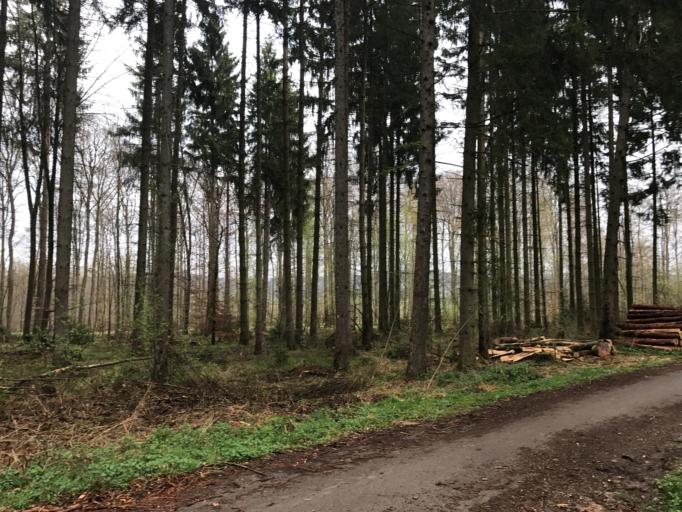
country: DE
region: Baden-Wuerttemberg
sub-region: Regierungsbezirk Stuttgart
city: Hochdorf
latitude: 48.6868
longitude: 9.4487
